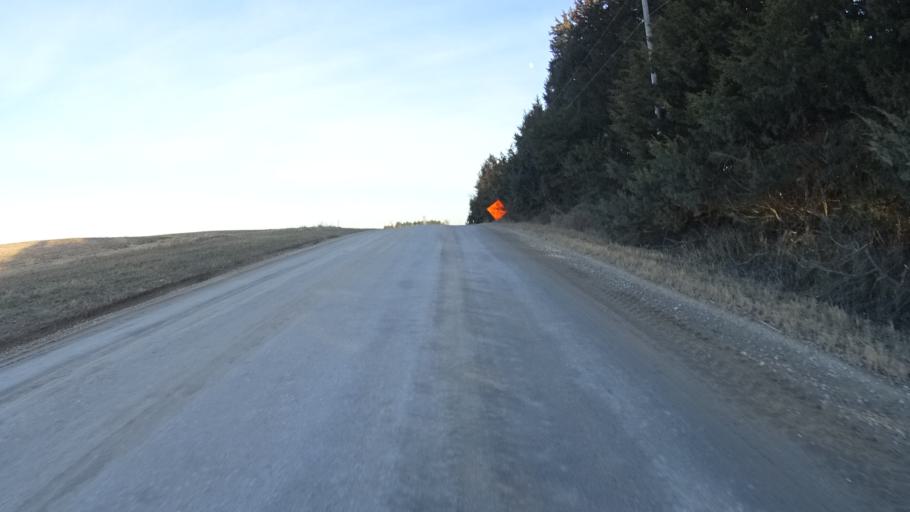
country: US
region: Nebraska
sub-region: Sarpy County
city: Springfield
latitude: 41.1326
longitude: -96.1146
